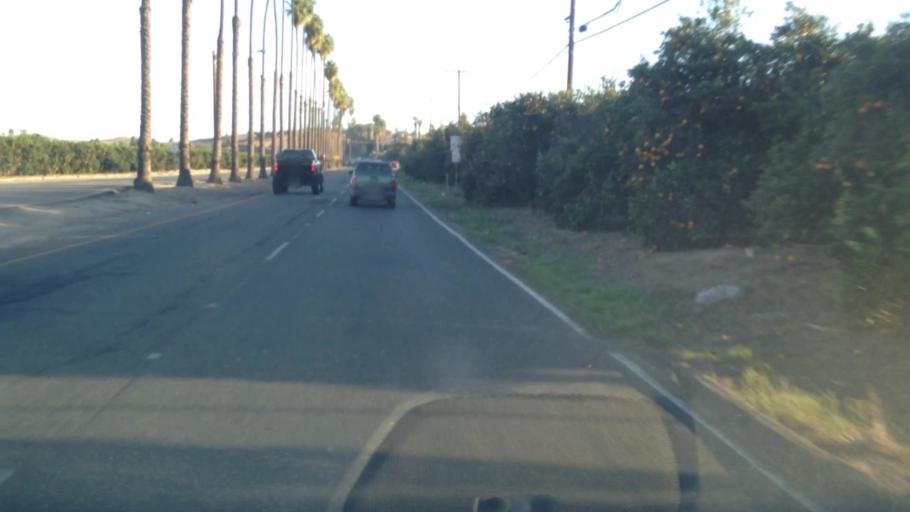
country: US
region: California
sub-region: Riverside County
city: Riverside
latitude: 33.8982
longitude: -117.4285
